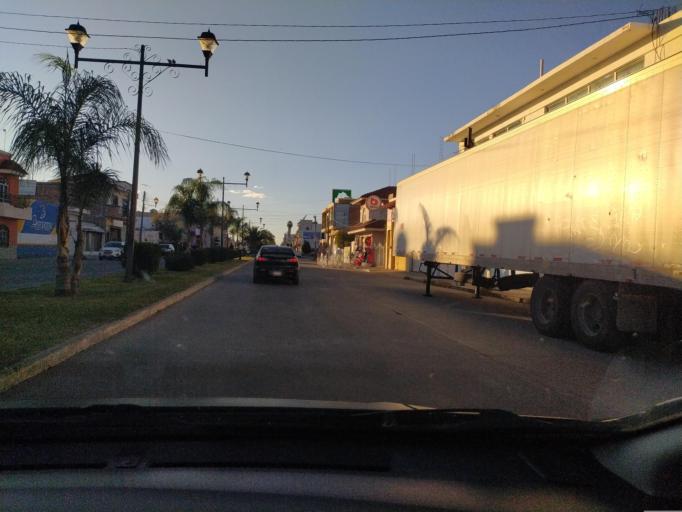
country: MX
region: Jalisco
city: San Julian
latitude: 21.0089
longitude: -102.1718
